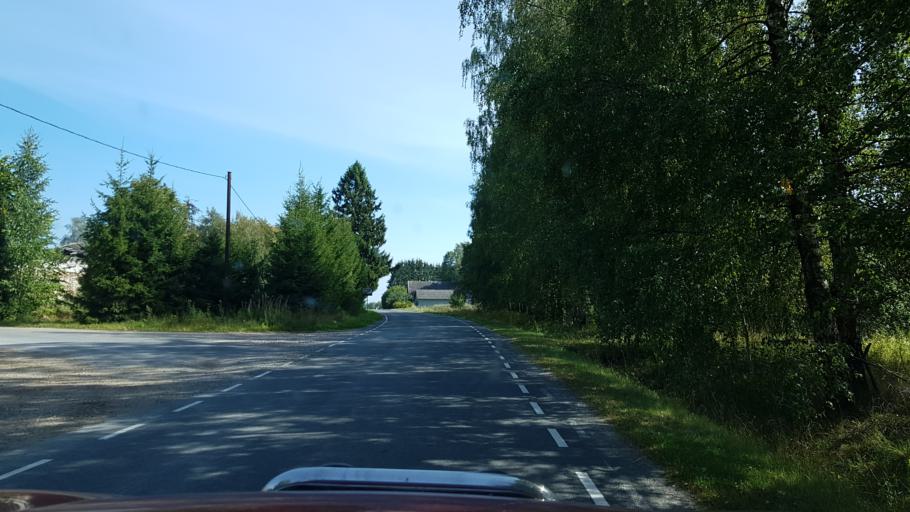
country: EE
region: Viljandimaa
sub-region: Suure-Jaani vald
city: Suure-Jaani
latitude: 58.4876
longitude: 25.5221
